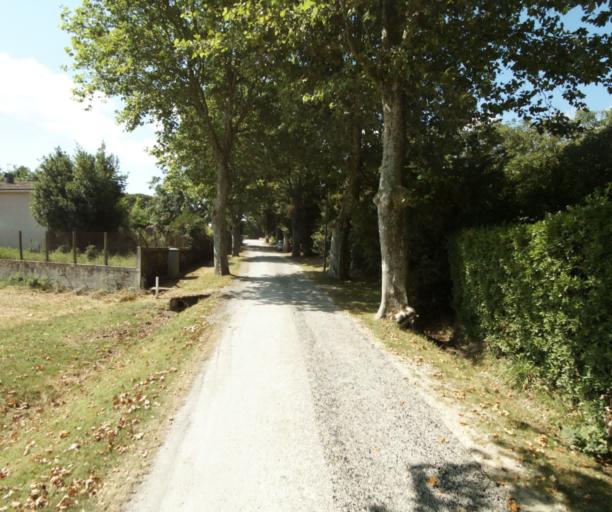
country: FR
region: Midi-Pyrenees
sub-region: Departement de la Haute-Garonne
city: Auriac-sur-Vendinelle
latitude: 43.4502
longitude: 1.7894
